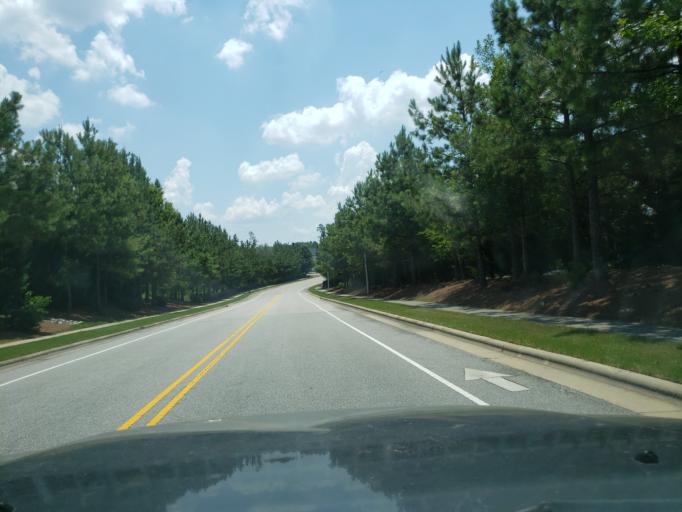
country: US
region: North Carolina
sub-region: Wake County
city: Green Level
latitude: 35.8389
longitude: -78.9135
